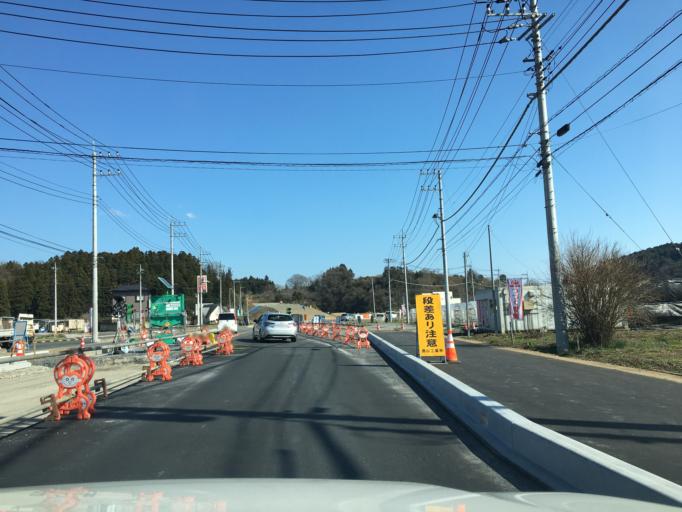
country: JP
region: Ibaraki
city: Omiya
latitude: 36.5567
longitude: 140.3177
